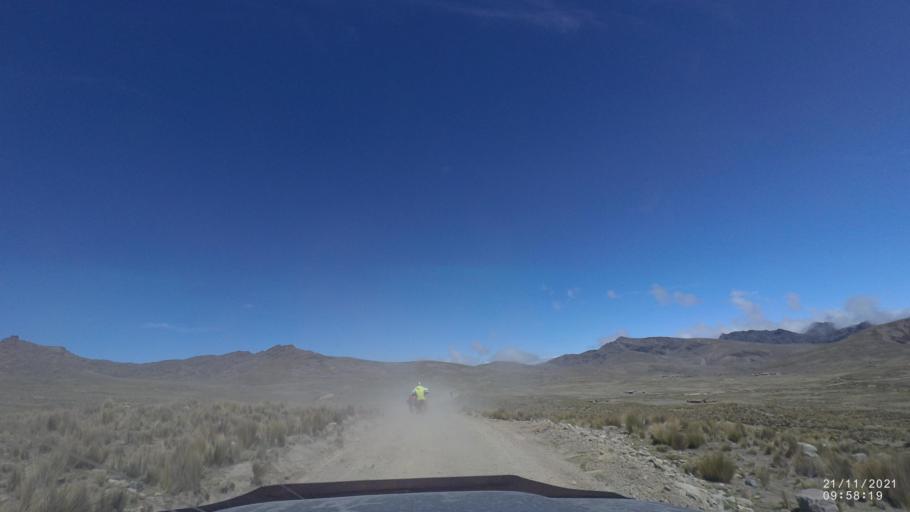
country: BO
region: Cochabamba
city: Cochabamba
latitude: -17.0369
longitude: -66.2760
